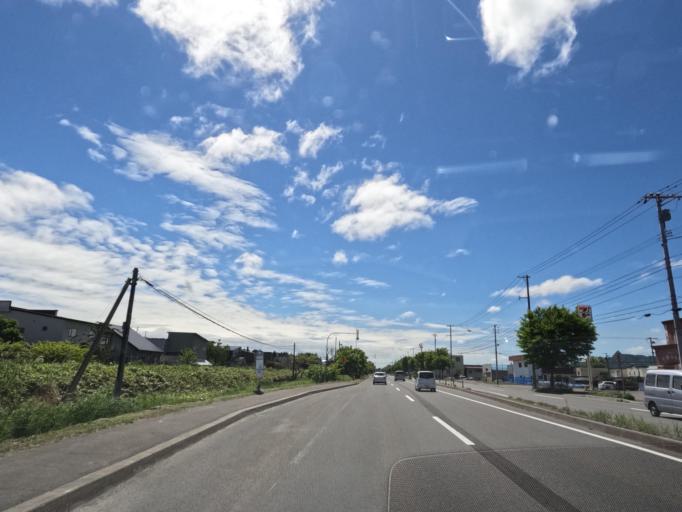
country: JP
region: Hokkaido
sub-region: Asahikawa-shi
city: Asahikawa
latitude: 43.7395
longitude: 142.3606
